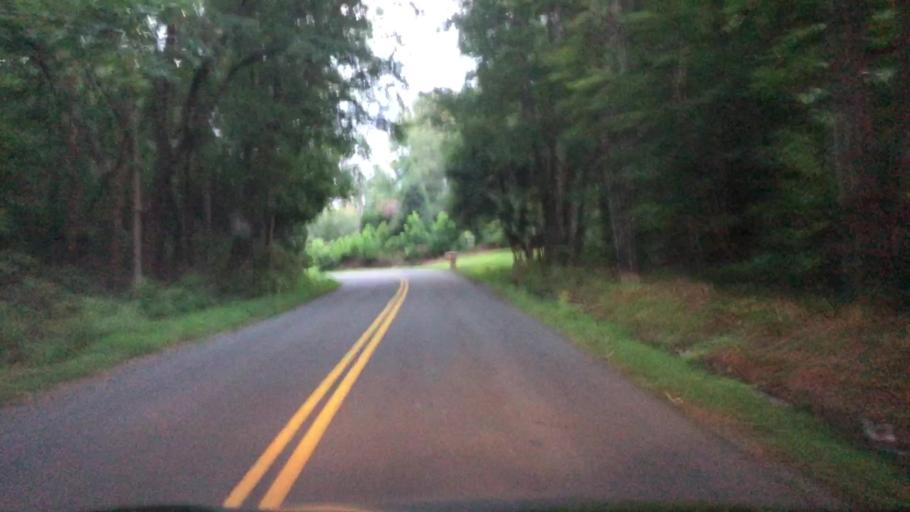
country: US
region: Virginia
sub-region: Stafford County
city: Falmouth
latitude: 38.4309
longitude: -77.5798
